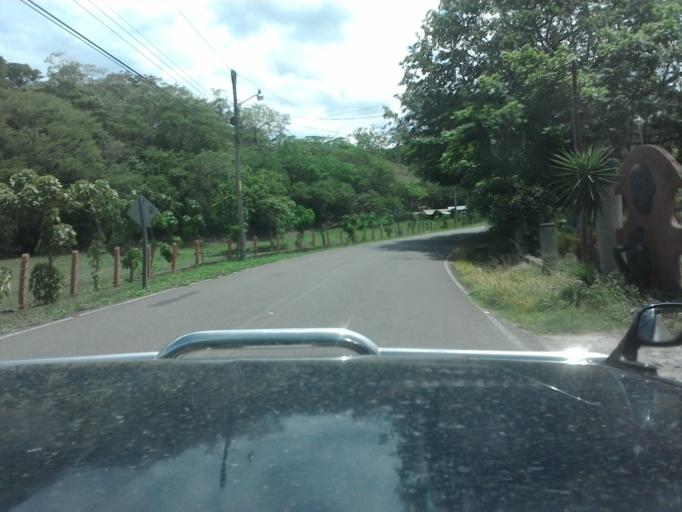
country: CR
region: Puntarenas
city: Miramar
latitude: 10.1287
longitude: -84.8340
